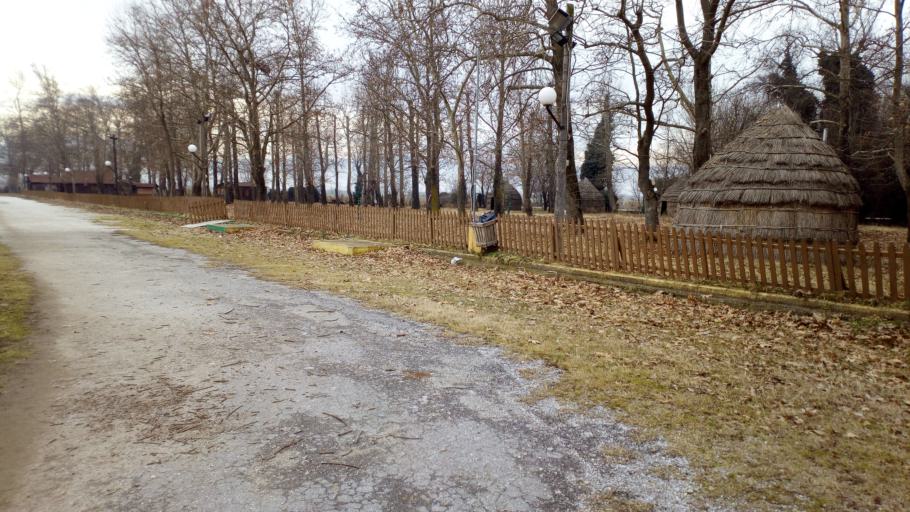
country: GR
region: Central Macedonia
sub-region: Nomos Thessalonikis
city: Lagkadas
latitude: 40.7344
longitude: 23.0837
